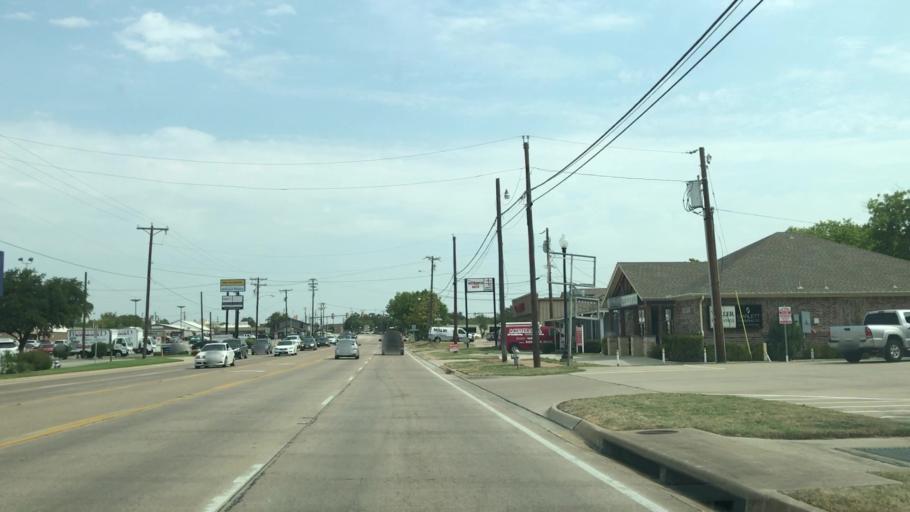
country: US
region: Texas
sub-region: Tarrant County
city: Keller
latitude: 32.9365
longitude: -97.2534
